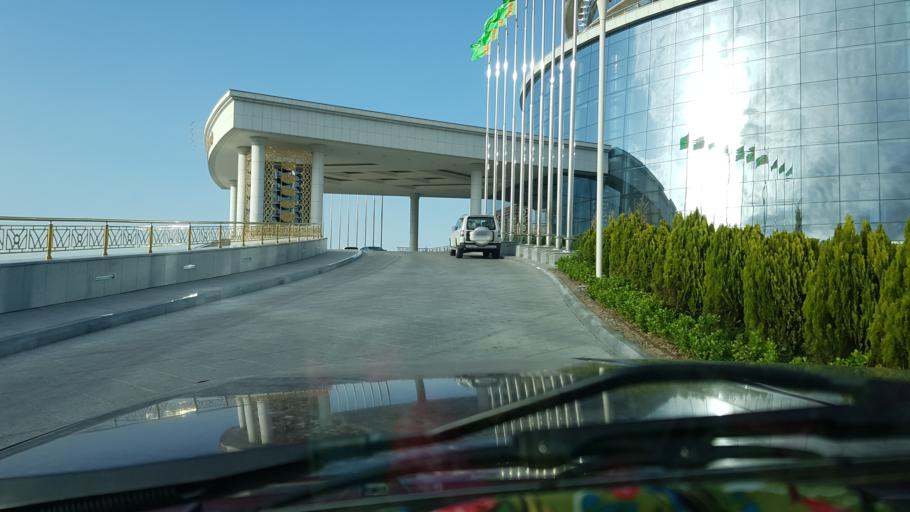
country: TM
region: Ahal
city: Ashgabat
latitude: 37.9290
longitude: 58.3325
